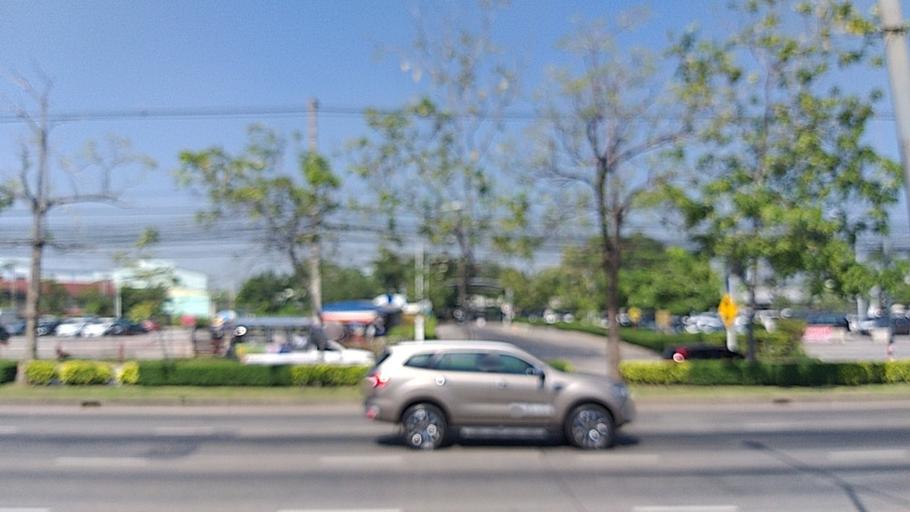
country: TH
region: Nakhon Ratchasima
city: Nakhon Ratchasima
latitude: 14.9872
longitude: 102.0952
